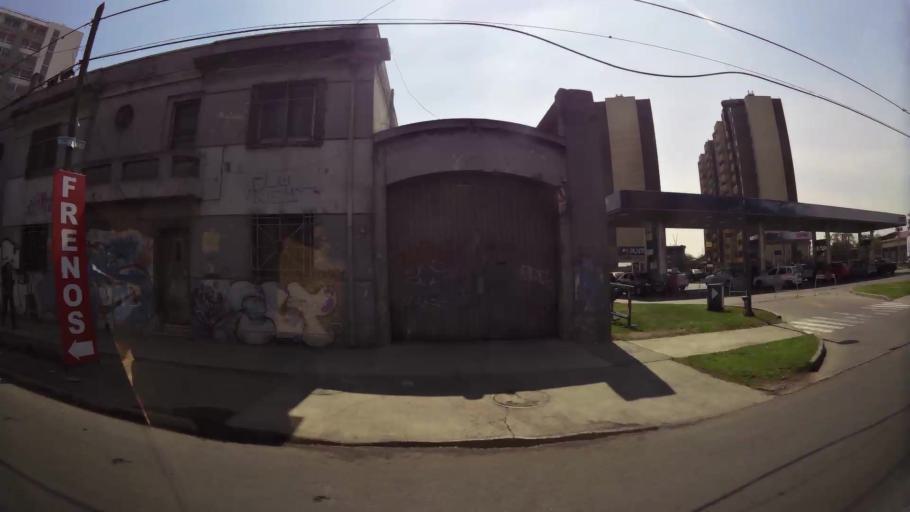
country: CL
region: Santiago Metropolitan
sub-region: Provincia de Santiago
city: Lo Prado
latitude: -33.4532
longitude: -70.6985
